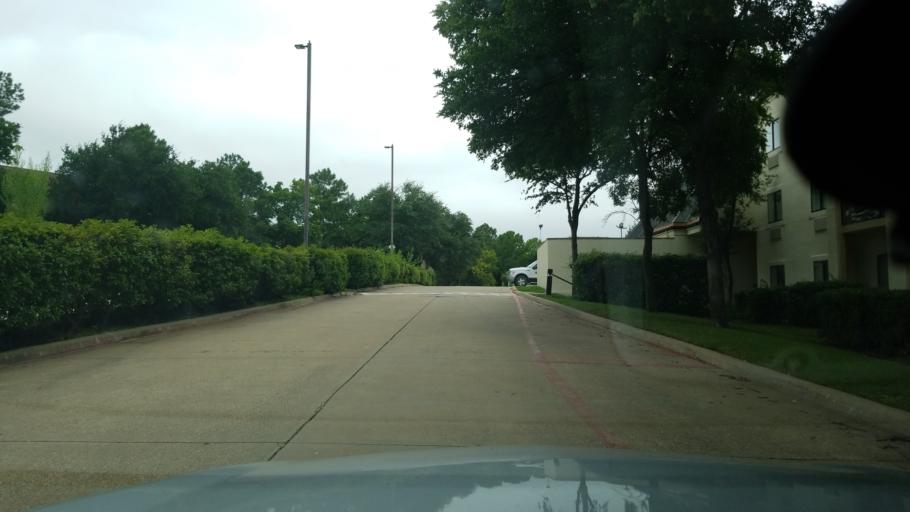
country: US
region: Texas
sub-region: Dallas County
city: Irving
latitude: 32.8680
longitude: -96.9462
